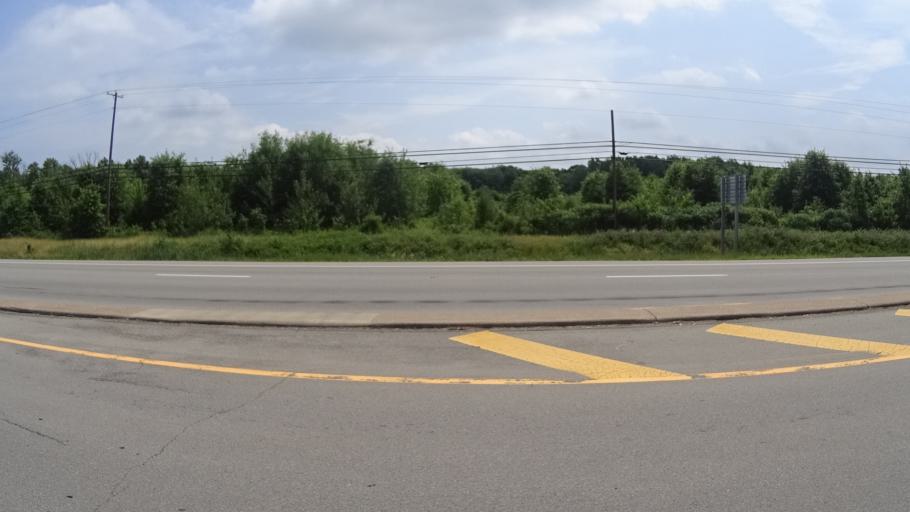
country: US
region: Ohio
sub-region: Lorain County
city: Vermilion
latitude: 41.3957
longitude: -82.3648
